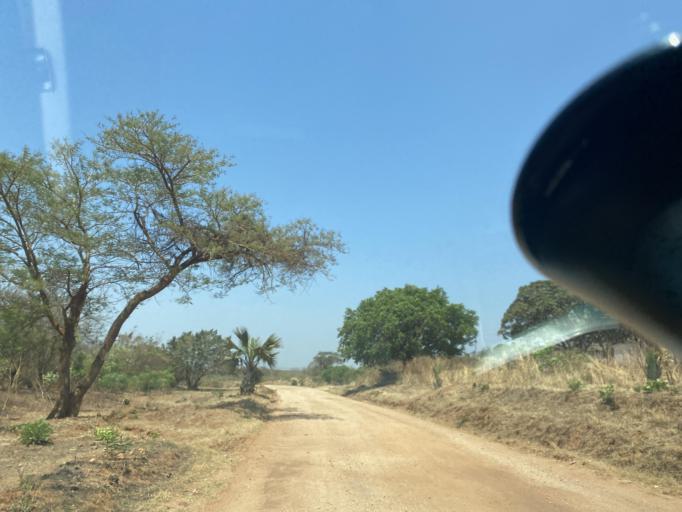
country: ZM
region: Lusaka
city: Lusaka
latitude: -15.5264
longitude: 28.1016
